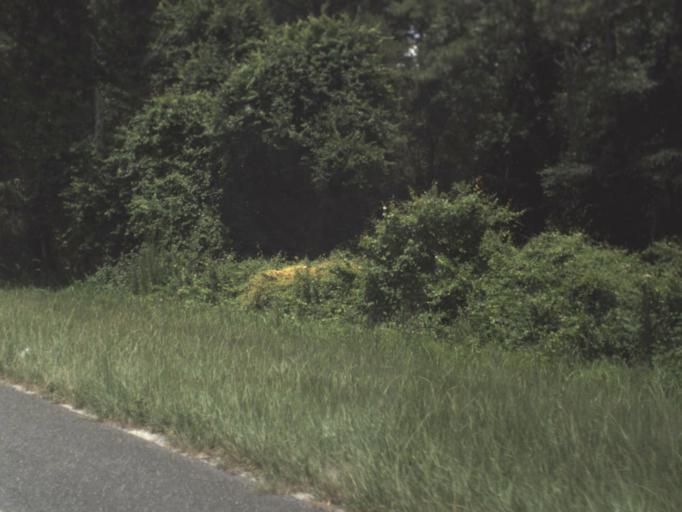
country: US
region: Florida
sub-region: Columbia County
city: Five Points
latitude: 30.2710
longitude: -82.6927
